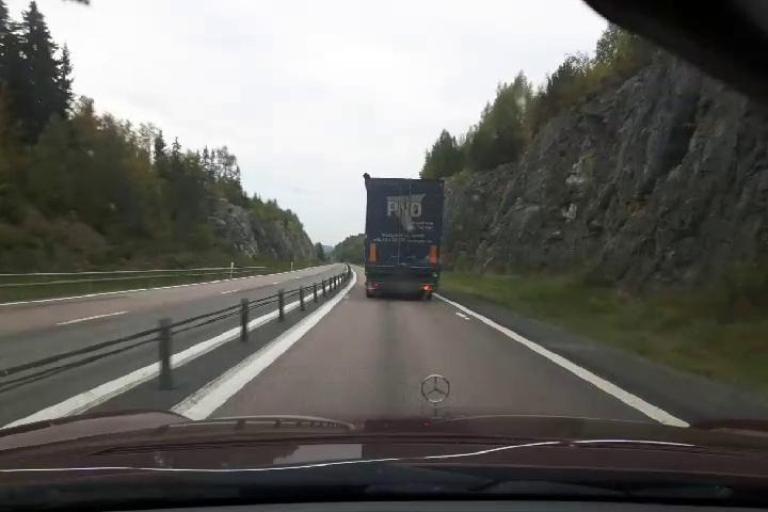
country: SE
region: Vaesternorrland
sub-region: Haernoesands Kommun
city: Haernoesand
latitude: 62.8292
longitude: 17.9680
